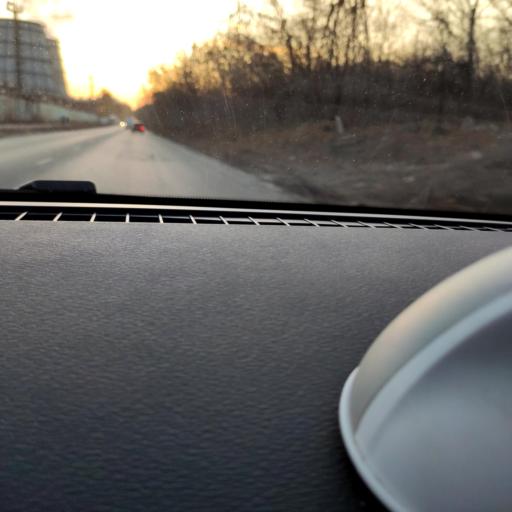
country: RU
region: Samara
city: Petra-Dubrava
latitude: 53.2537
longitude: 50.2756
